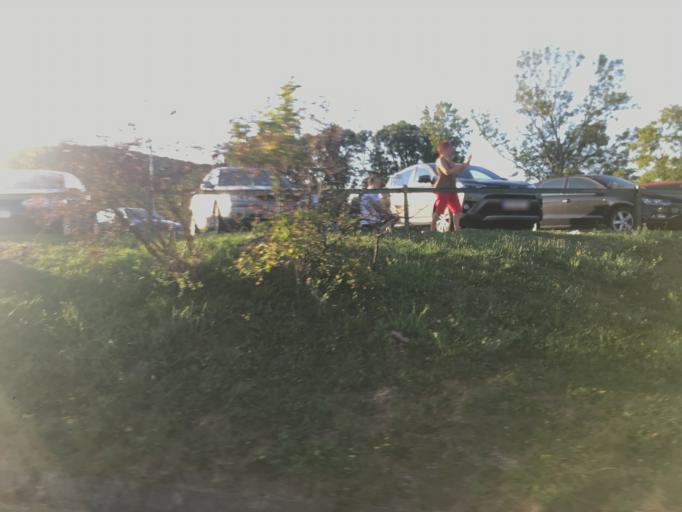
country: AT
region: Lower Austria
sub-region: Politischer Bezirk Wien-Umgebung
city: Klosterneuburg
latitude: 48.2636
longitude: 16.3226
